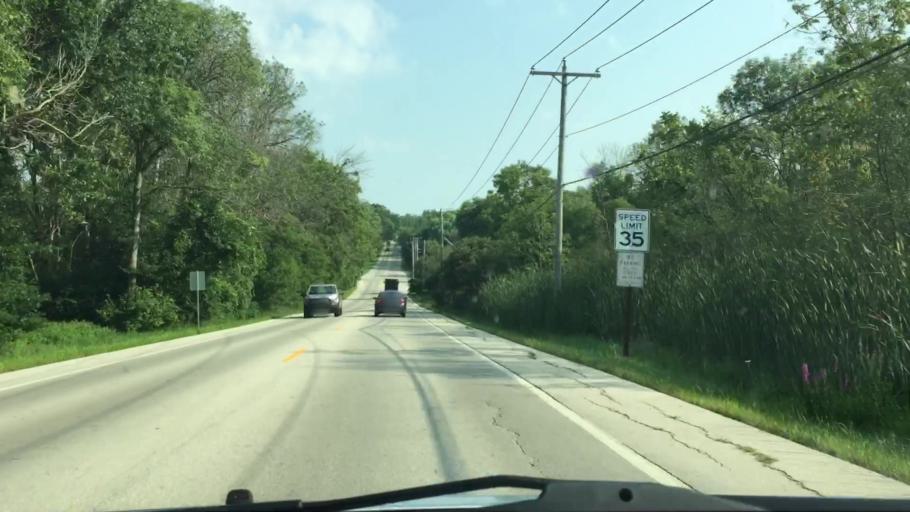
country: US
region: Wisconsin
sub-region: Waukesha County
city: Brookfield
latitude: 43.0451
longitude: -88.1465
